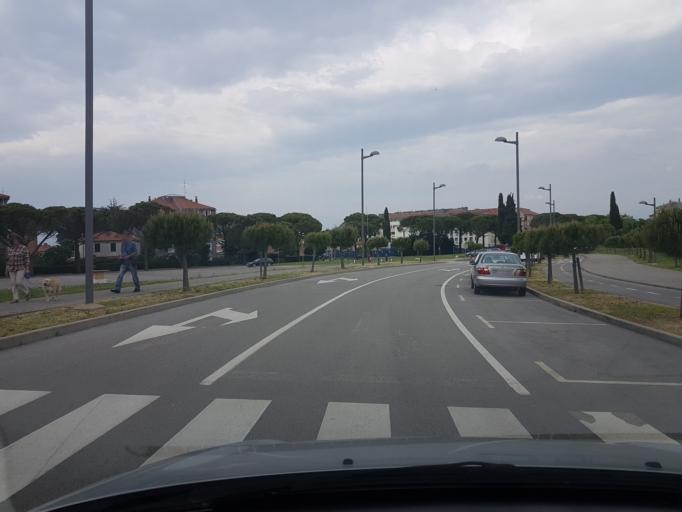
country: SI
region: Izola-Isola
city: Izola
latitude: 45.5310
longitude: 13.6582
